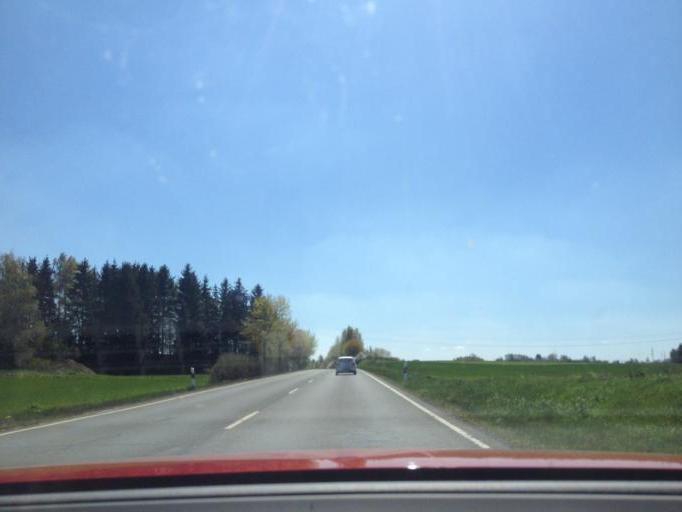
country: DE
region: Bavaria
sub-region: Upper Franconia
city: Schwarzenbach an der Saale
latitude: 50.2386
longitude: 11.9348
